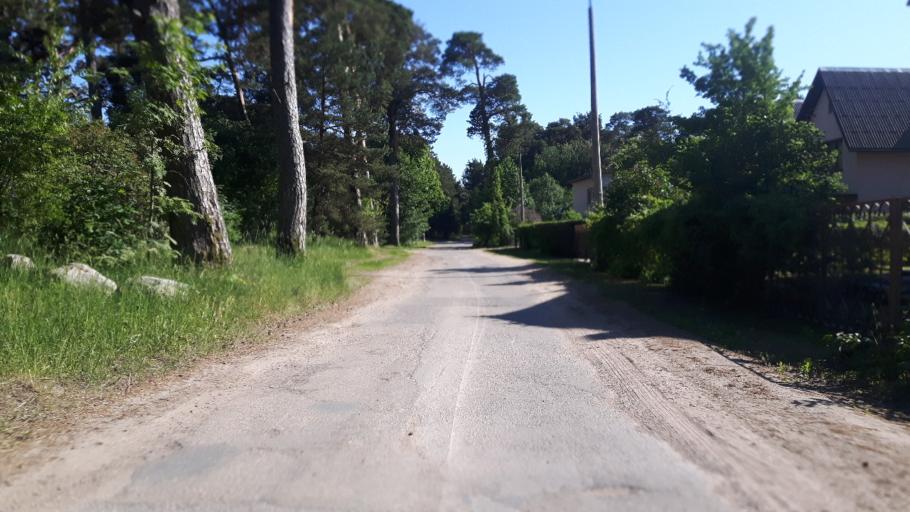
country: LV
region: Salacgrivas
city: Salacgriva
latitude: 57.7447
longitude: 24.3528
